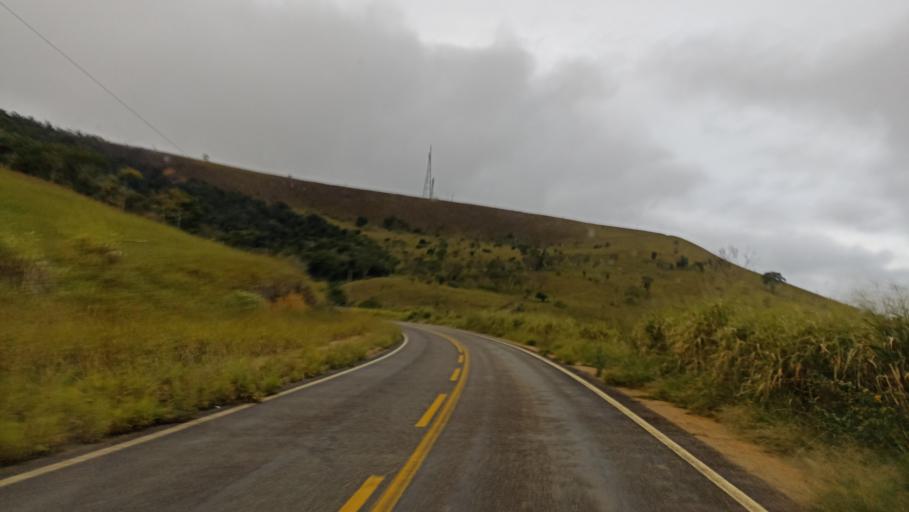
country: BR
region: Minas Gerais
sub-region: Joaima
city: Joaima
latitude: -16.6795
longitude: -40.5232
